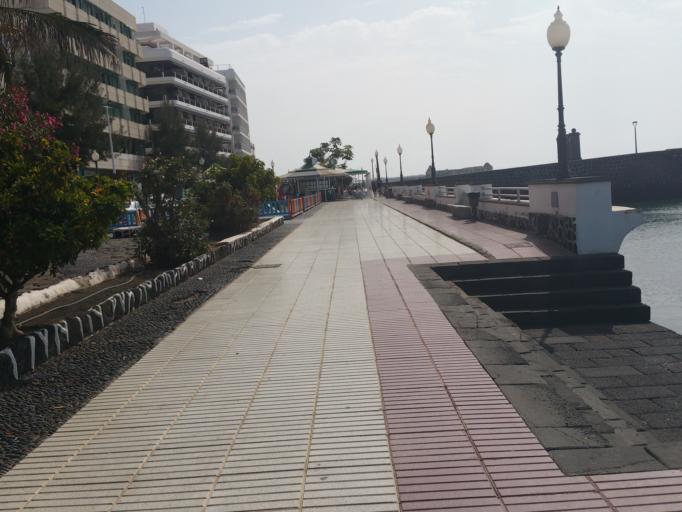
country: ES
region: Canary Islands
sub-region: Provincia de Las Palmas
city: Arrecife
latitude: 28.9580
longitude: -13.5489
